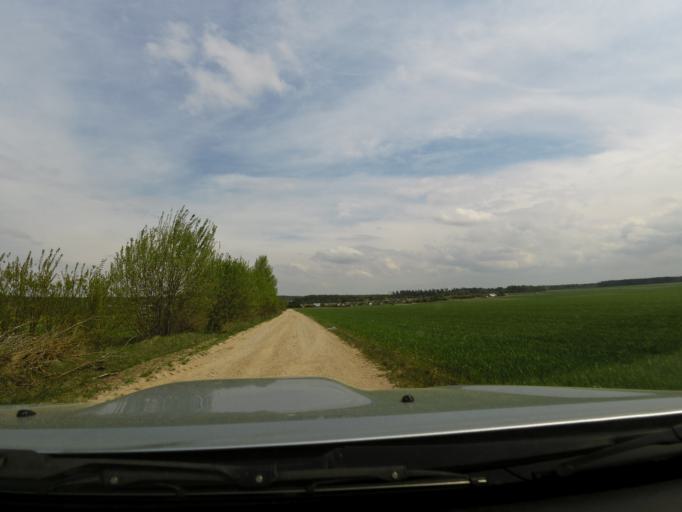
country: LT
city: Salcininkai
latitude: 54.4167
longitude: 25.3123
